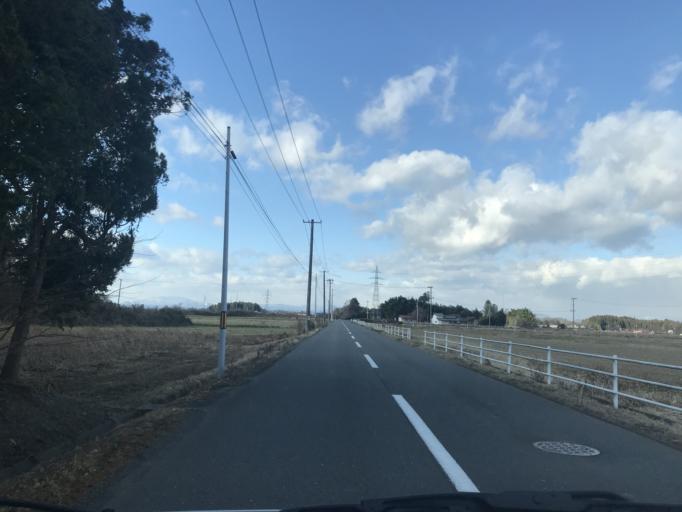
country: JP
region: Miyagi
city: Kogota
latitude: 38.7395
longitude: 141.0518
